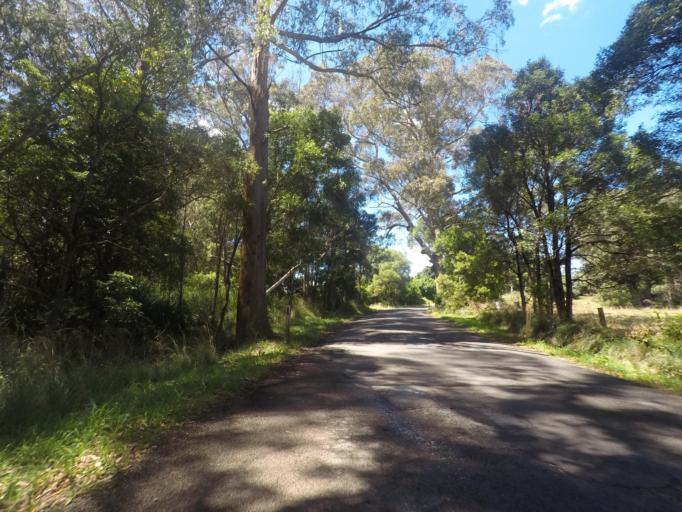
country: AU
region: New South Wales
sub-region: Shellharbour
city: Calderwood
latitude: -34.5608
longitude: 150.5889
